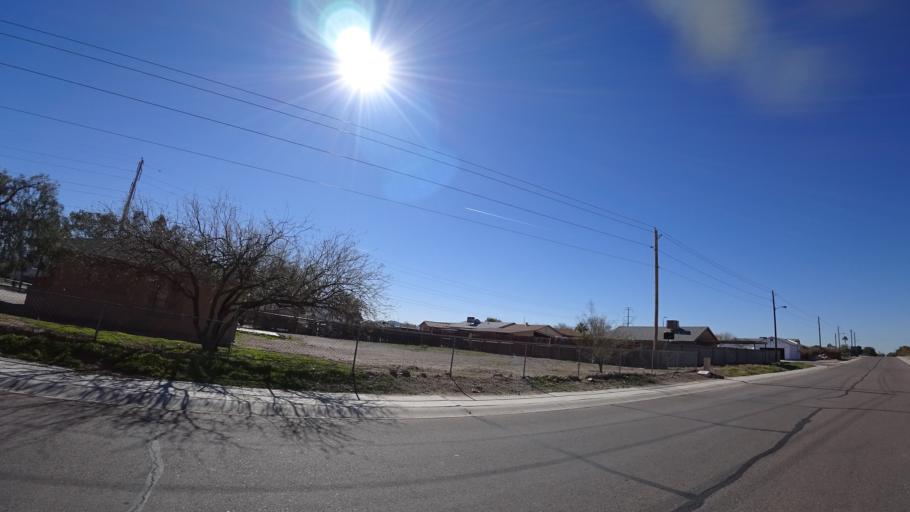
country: US
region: Arizona
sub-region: Maricopa County
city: Avondale
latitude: 33.4134
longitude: -112.3249
